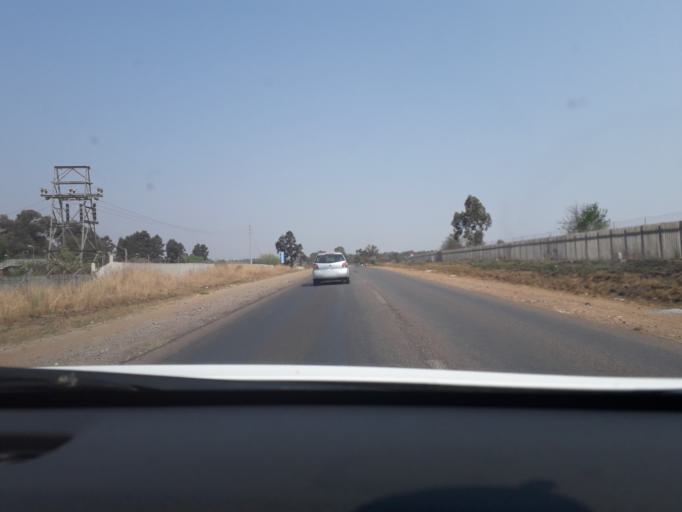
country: ZA
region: Gauteng
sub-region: City of Tshwane Metropolitan Municipality
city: Centurion
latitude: -25.9131
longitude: 28.2280
